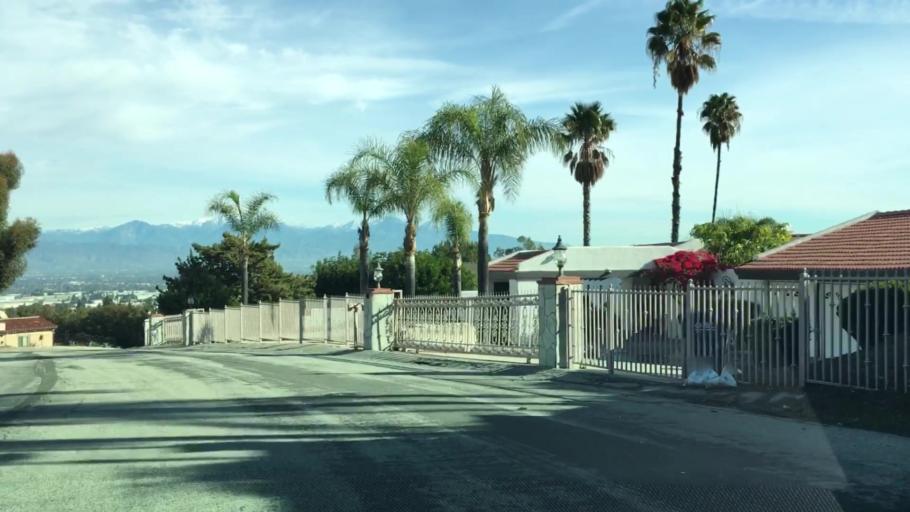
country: US
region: California
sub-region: Los Angeles County
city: Hacienda Heights
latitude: 34.0078
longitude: -117.9865
